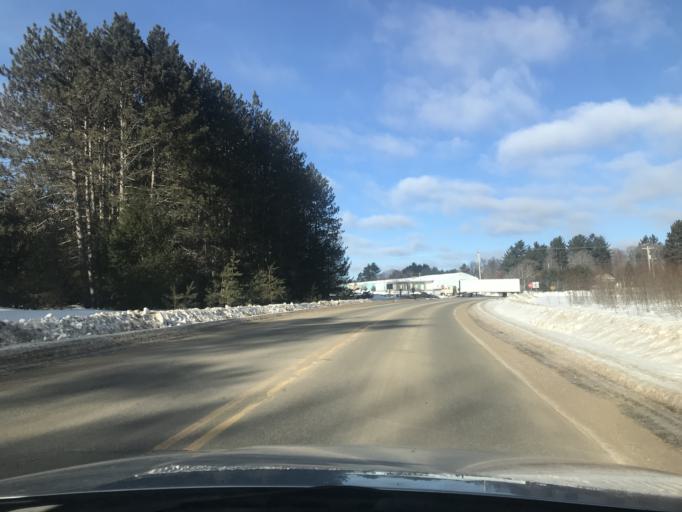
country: US
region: Wisconsin
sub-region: Marinette County
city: Niagara
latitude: 45.6392
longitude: -87.9783
